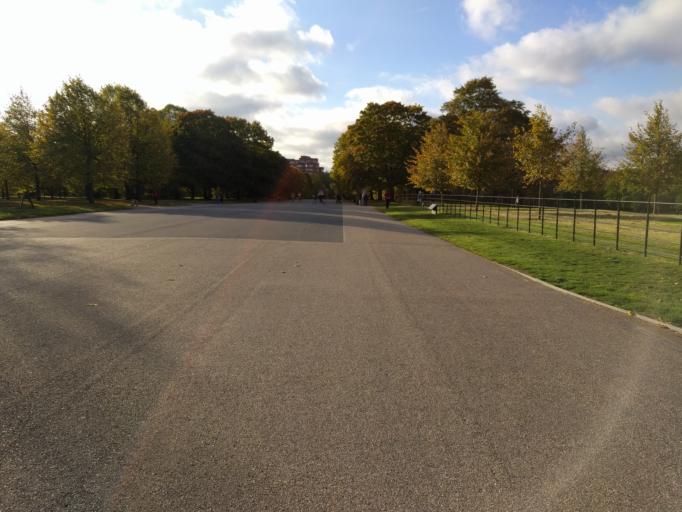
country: GB
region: England
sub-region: Greater London
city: Bayswater
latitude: 51.5051
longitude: -0.1857
